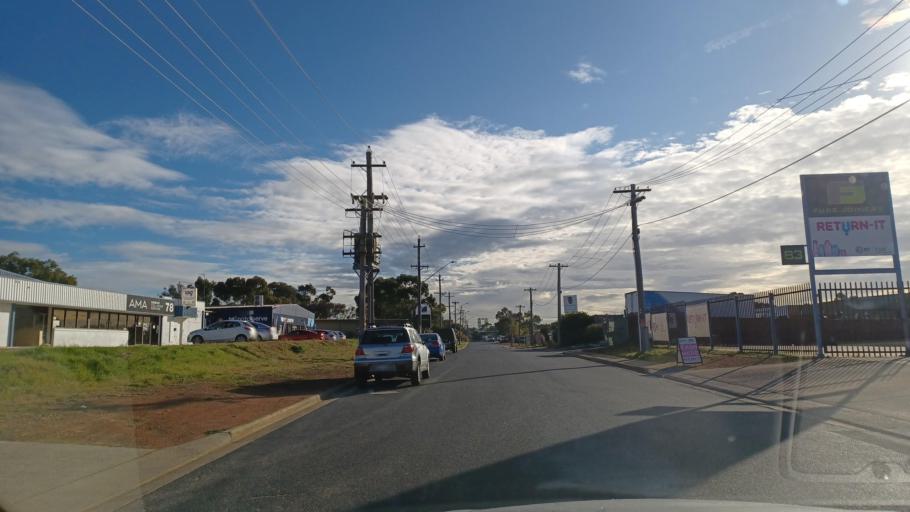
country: AU
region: Australian Capital Territory
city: Kaleen
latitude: -35.2195
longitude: 149.1380
